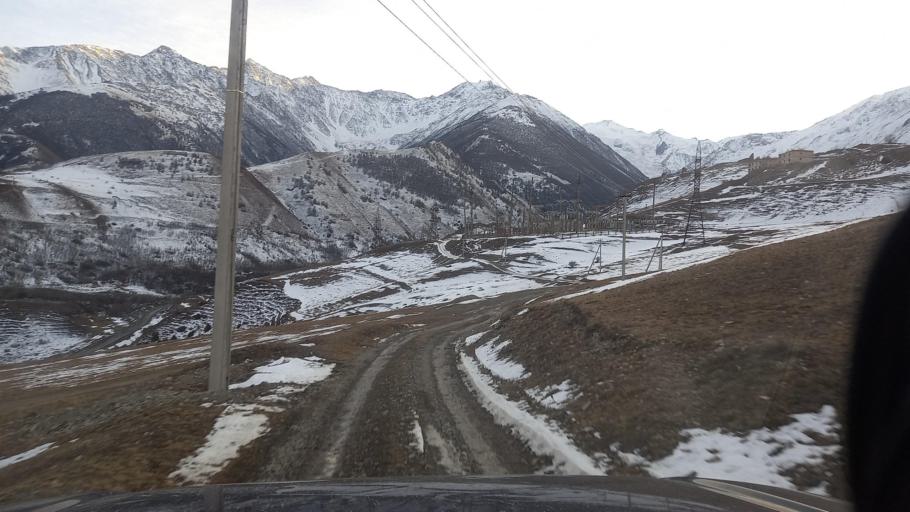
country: RU
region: Ingushetiya
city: Dzhayrakh
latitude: 42.8482
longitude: 44.5134
